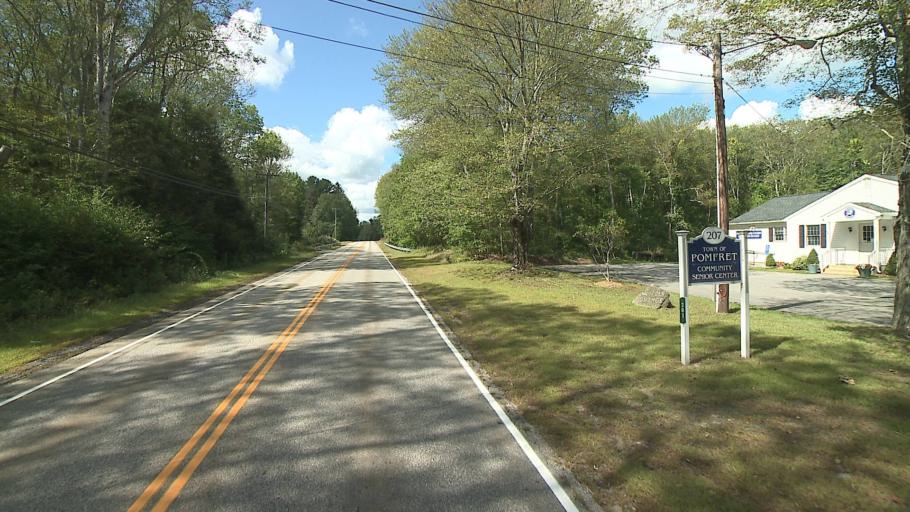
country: US
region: Connecticut
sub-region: Windham County
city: South Woodstock
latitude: 41.8614
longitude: -71.9771
